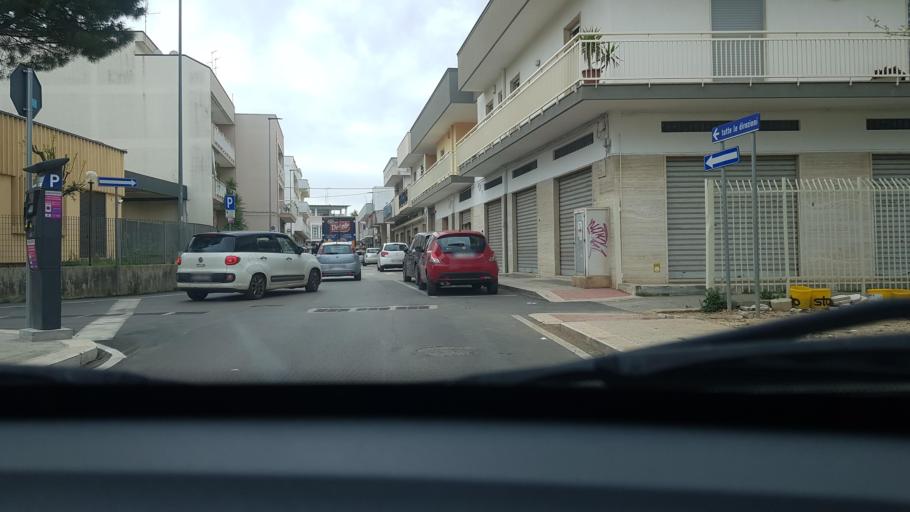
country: IT
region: Apulia
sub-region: Provincia di Bari
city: Noicattaro
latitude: 41.0335
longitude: 16.9831
